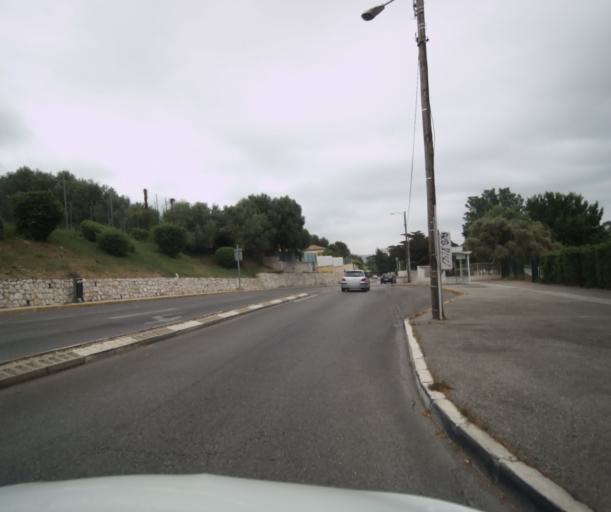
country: FR
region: Provence-Alpes-Cote d'Azur
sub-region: Departement du Var
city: Ollioules
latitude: 43.1396
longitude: 5.8834
